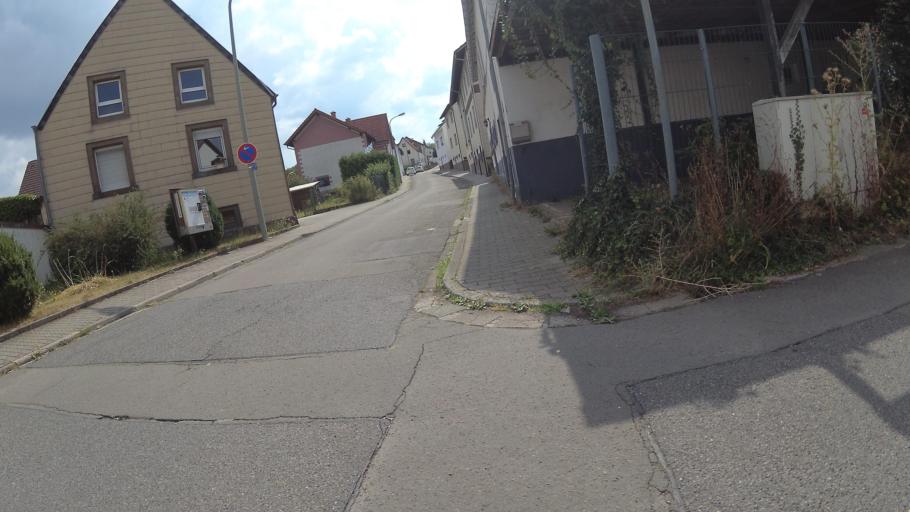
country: DE
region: Rheinland-Pfalz
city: Althornbach
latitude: 49.2181
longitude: 7.3763
